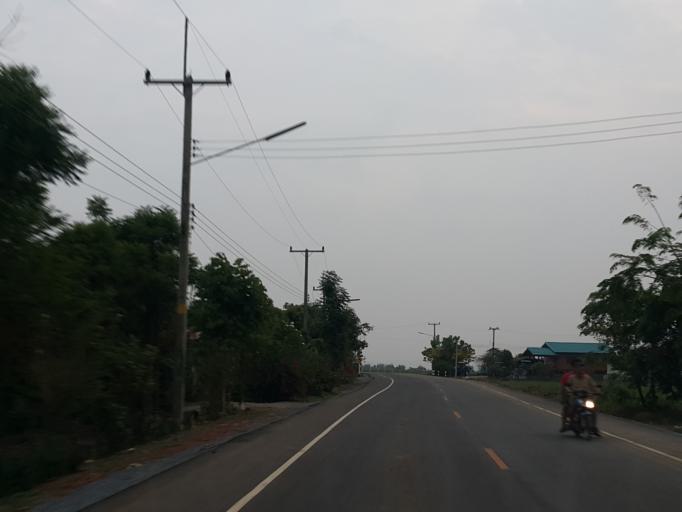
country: TH
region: Suphan Buri
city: Dan Chang
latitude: 14.9356
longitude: 99.6407
